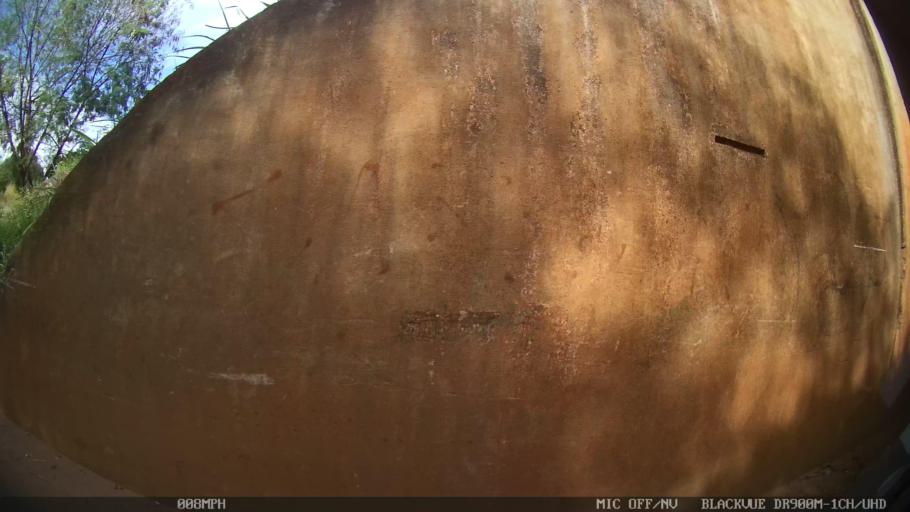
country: BR
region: Sao Paulo
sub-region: Sao Jose Do Rio Preto
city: Sao Jose do Rio Preto
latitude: -20.8425
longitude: -49.3353
